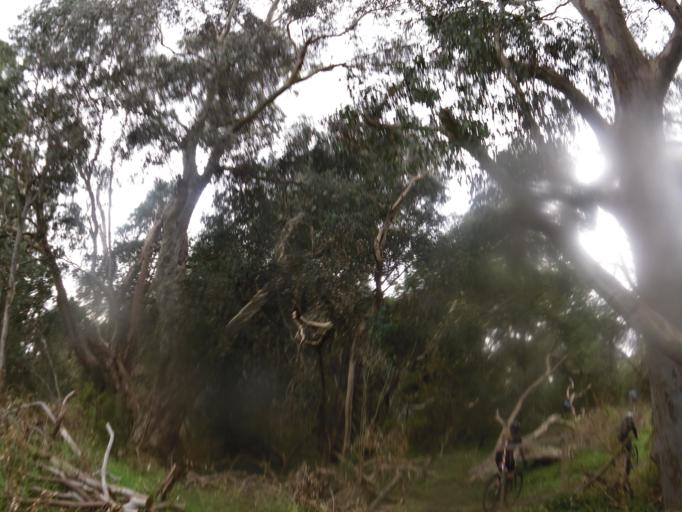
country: AU
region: Victoria
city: Ivanhoe East
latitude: -37.7766
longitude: 145.0675
